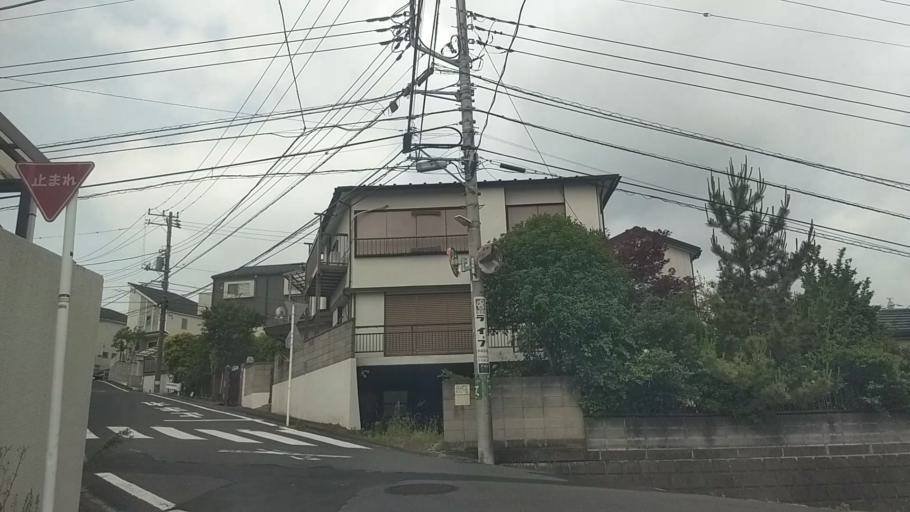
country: JP
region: Kanagawa
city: Fujisawa
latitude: 35.3837
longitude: 139.5175
